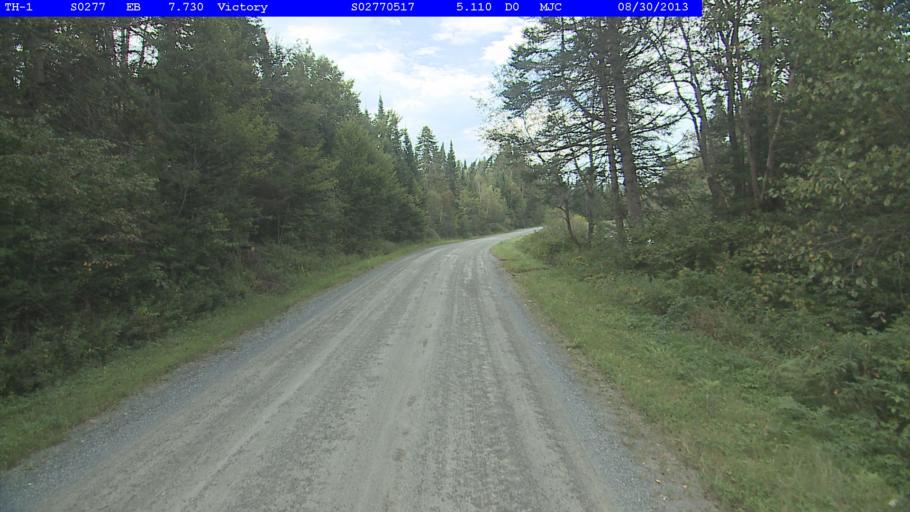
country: US
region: Vermont
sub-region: Caledonia County
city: Lyndonville
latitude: 44.5428
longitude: -71.7866
